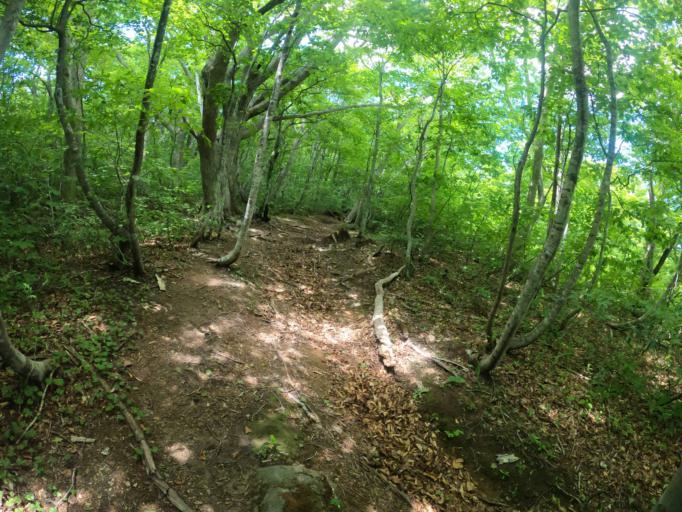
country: JP
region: Iwate
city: Ichinoseki
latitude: 38.9239
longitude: 140.7965
